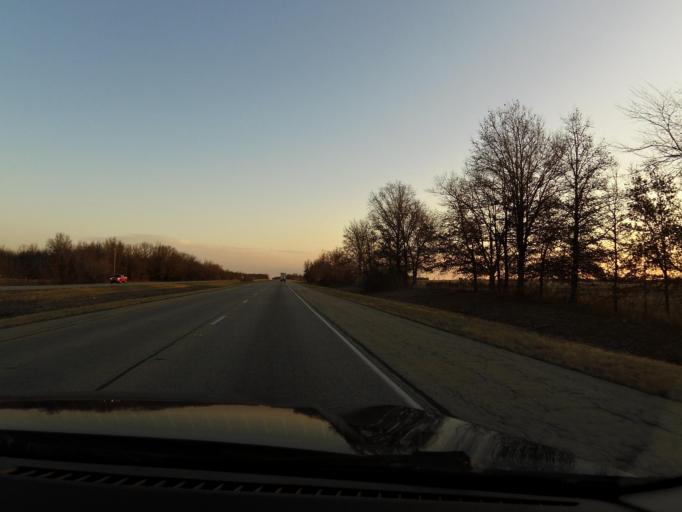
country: US
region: Illinois
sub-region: Marion County
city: Salem
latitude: 38.6984
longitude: -88.9583
